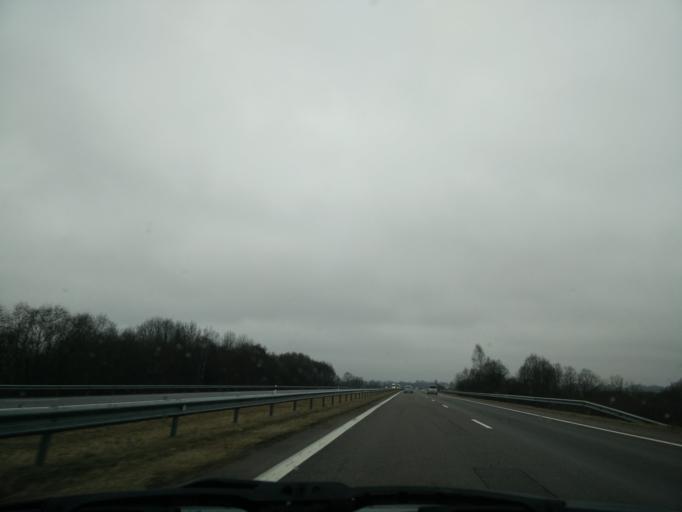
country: LT
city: Skaudvile
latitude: 55.4357
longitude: 22.7394
